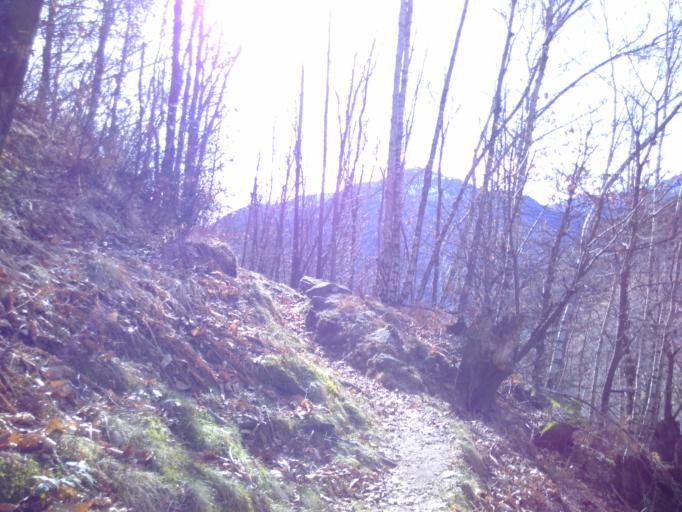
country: CH
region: Ticino
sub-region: Locarno District
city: Verscio
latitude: 46.2576
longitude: 8.7216
